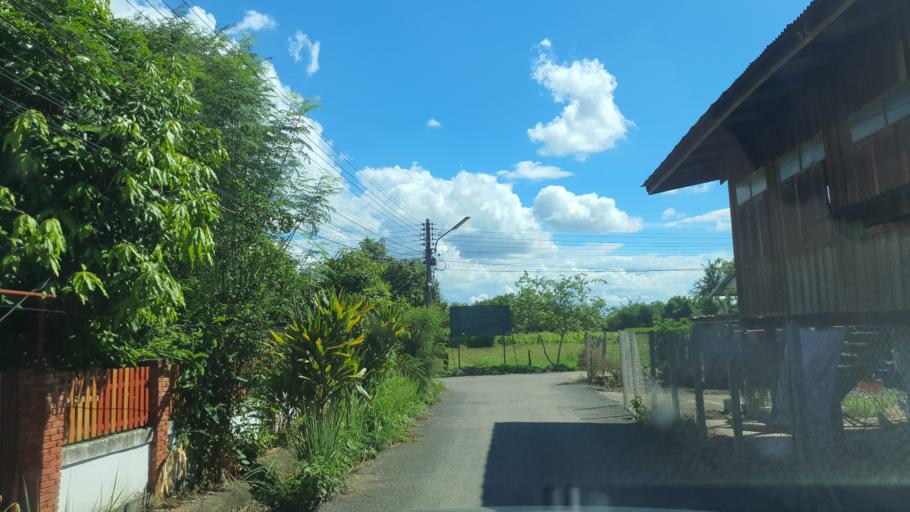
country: TH
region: Chiang Mai
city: Mae On
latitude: 18.7677
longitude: 99.2558
